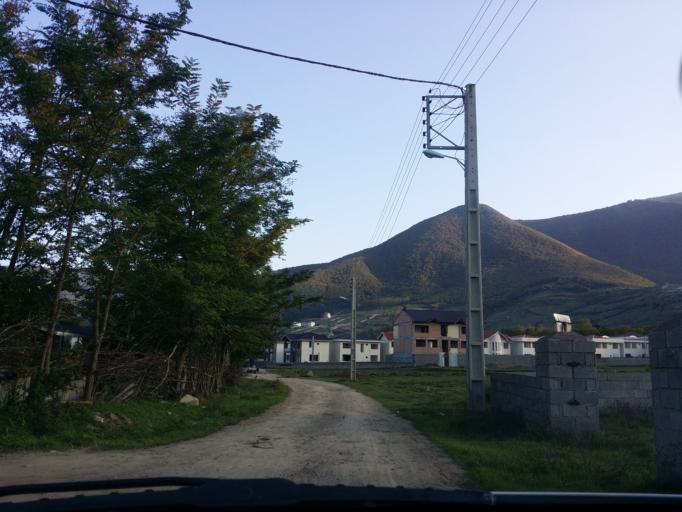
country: IR
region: Mazandaran
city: `Abbasabad
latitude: 36.5130
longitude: 51.1820
